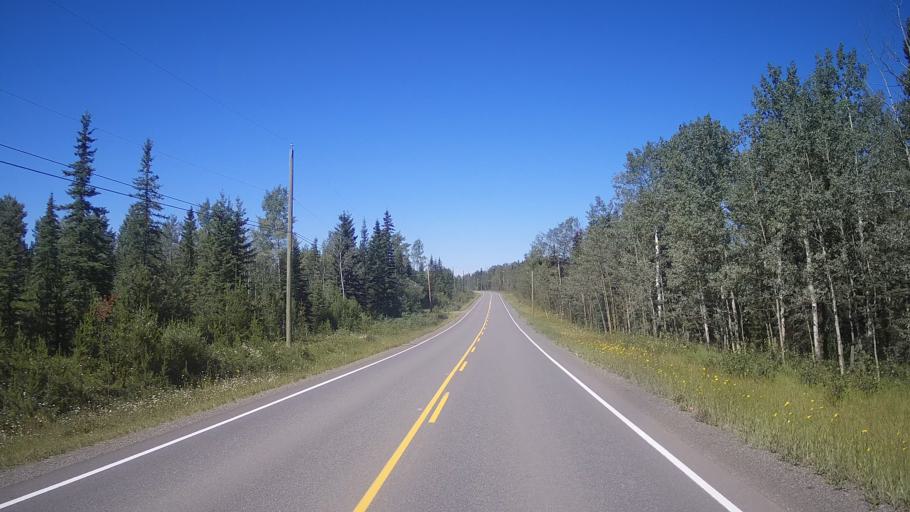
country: CA
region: British Columbia
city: Cache Creek
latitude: 51.5454
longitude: -120.9357
